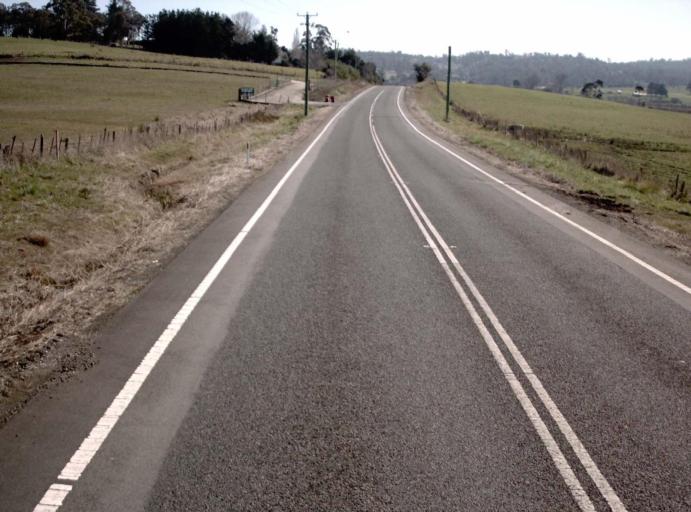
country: AU
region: Tasmania
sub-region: Launceston
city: Mayfield
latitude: -41.3234
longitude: 147.0625
